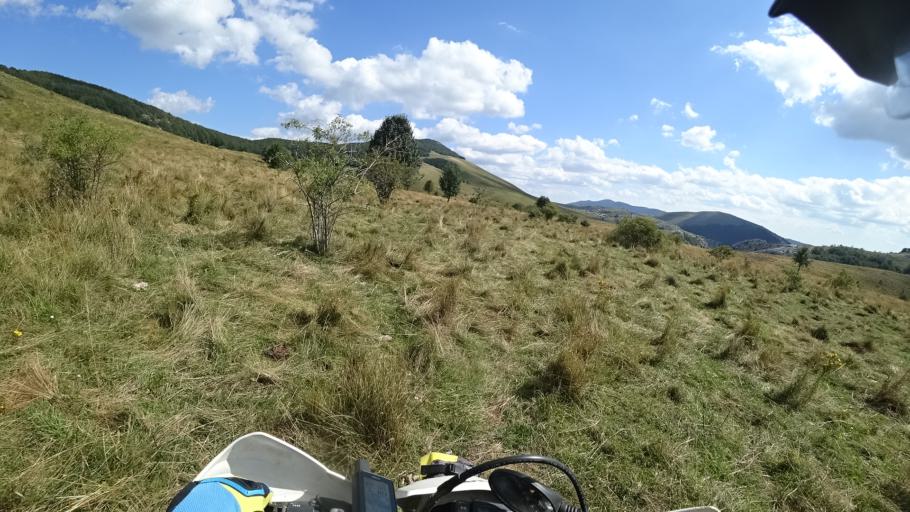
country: HR
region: Zadarska
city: Gracac
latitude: 44.4193
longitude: 15.9989
